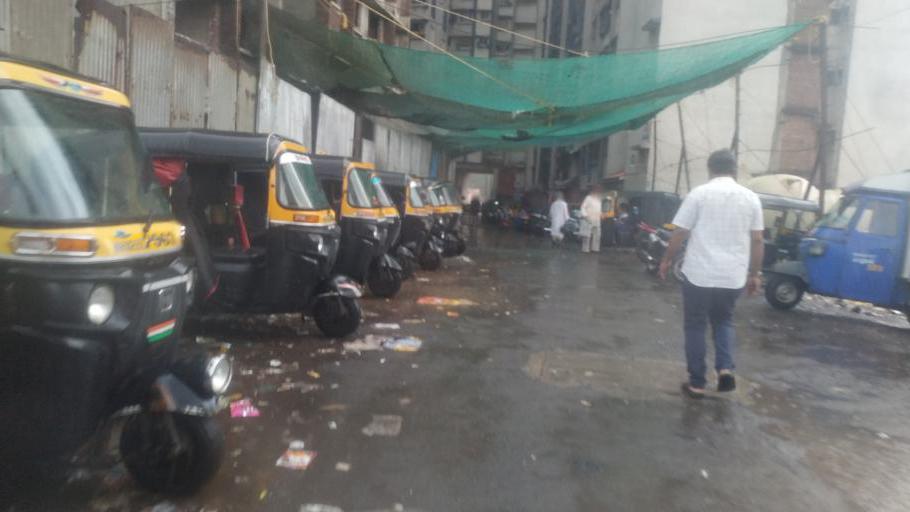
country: IN
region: Maharashtra
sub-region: Mumbai Suburban
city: Mumbai
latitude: 19.0642
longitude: 72.8562
